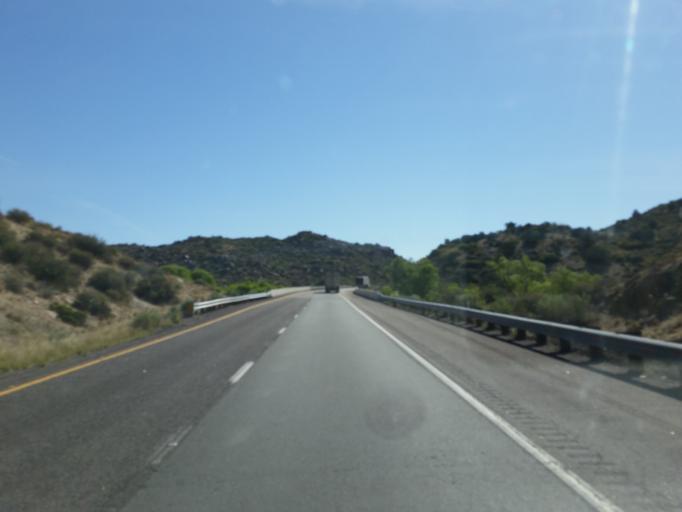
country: US
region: Arizona
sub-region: Mohave County
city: Peach Springs
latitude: 35.1739
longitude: -113.5011
